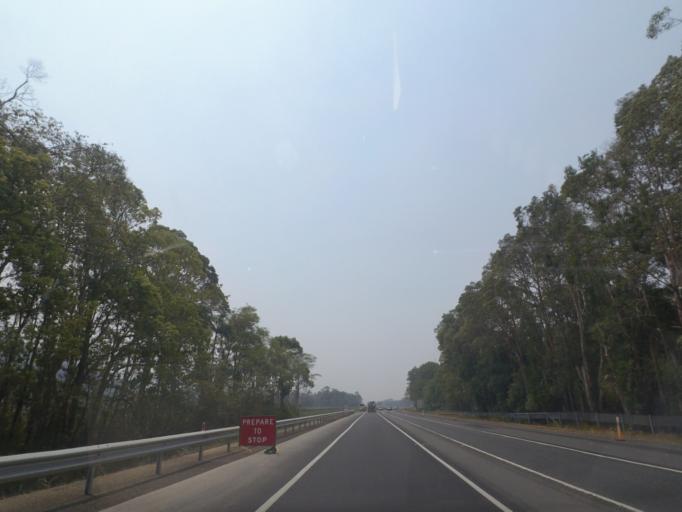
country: AU
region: New South Wales
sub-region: Ballina
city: Ballina
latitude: -28.9179
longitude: 153.4769
